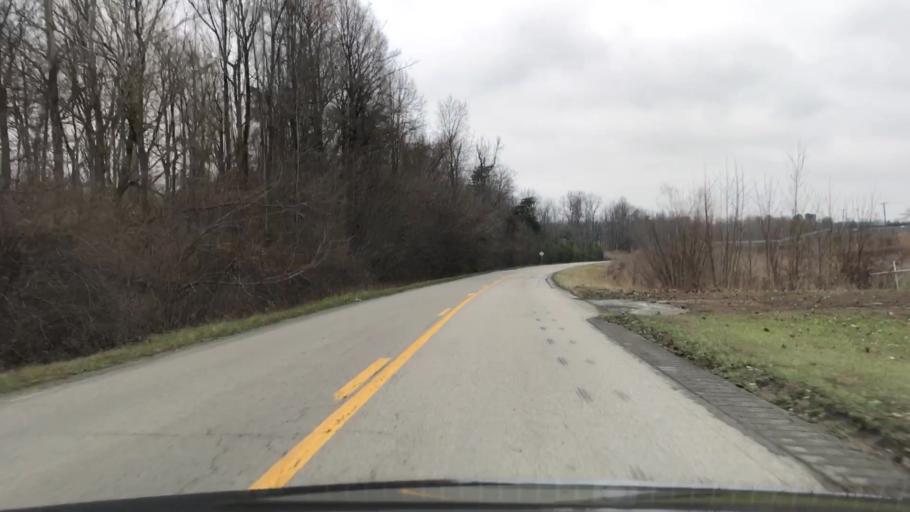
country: US
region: Kentucky
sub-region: Muhlenberg County
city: Morehead
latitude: 37.2631
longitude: -87.2109
